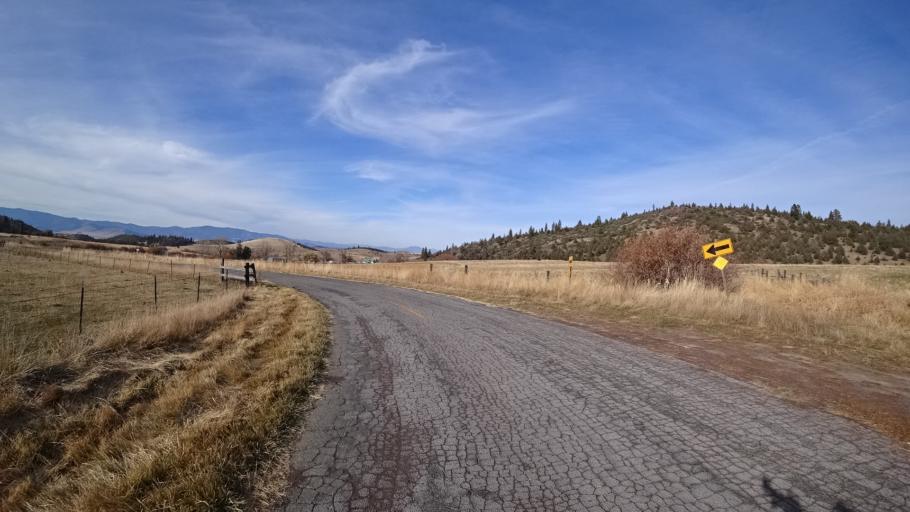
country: US
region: California
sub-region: Siskiyou County
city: Weed
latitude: 41.4612
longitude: -122.3842
